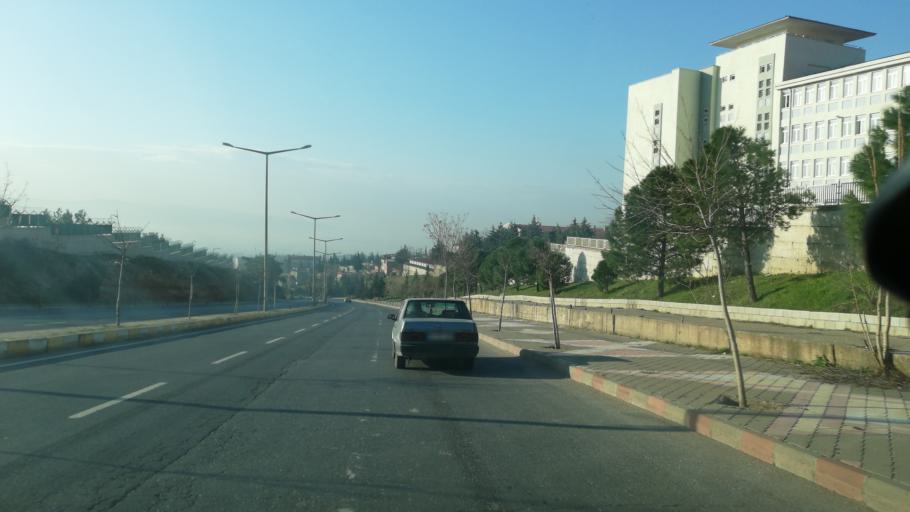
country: TR
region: Kahramanmaras
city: Kahramanmaras
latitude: 37.5981
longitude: 36.9252
